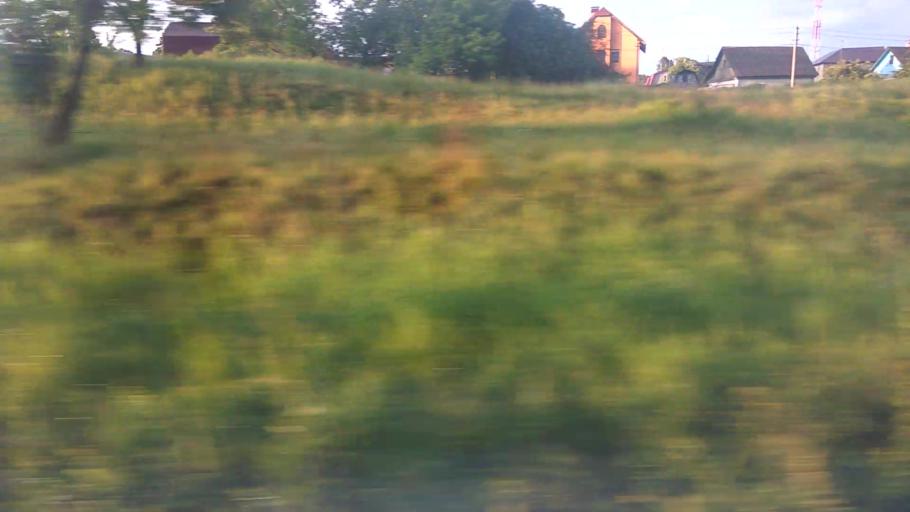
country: RU
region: Moskovskaya
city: Kashira
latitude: 54.8700
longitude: 38.1252
